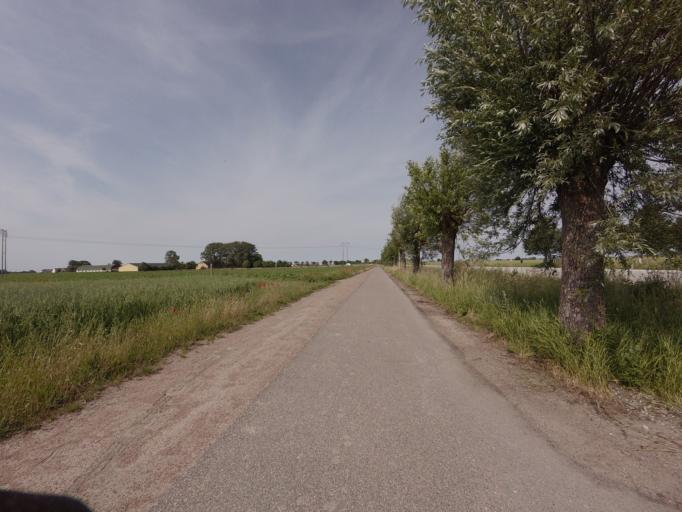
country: SE
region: Skane
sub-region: Malmo
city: Bunkeflostrand
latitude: 55.5282
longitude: 12.9677
